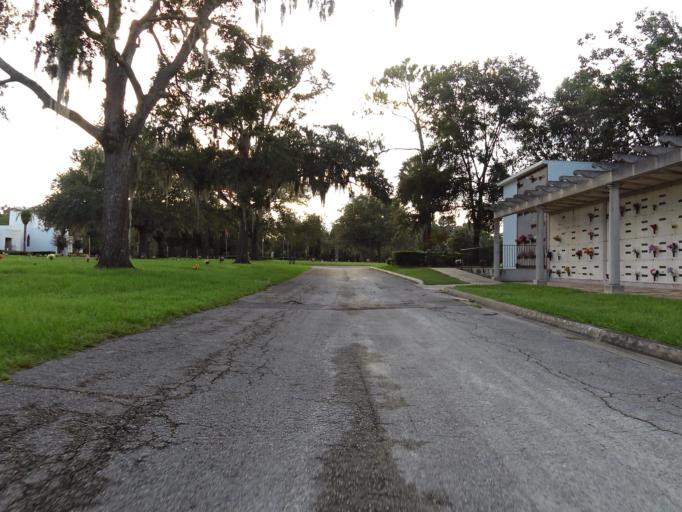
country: US
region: Florida
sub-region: Duval County
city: Jacksonville
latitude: 30.2967
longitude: -81.6203
